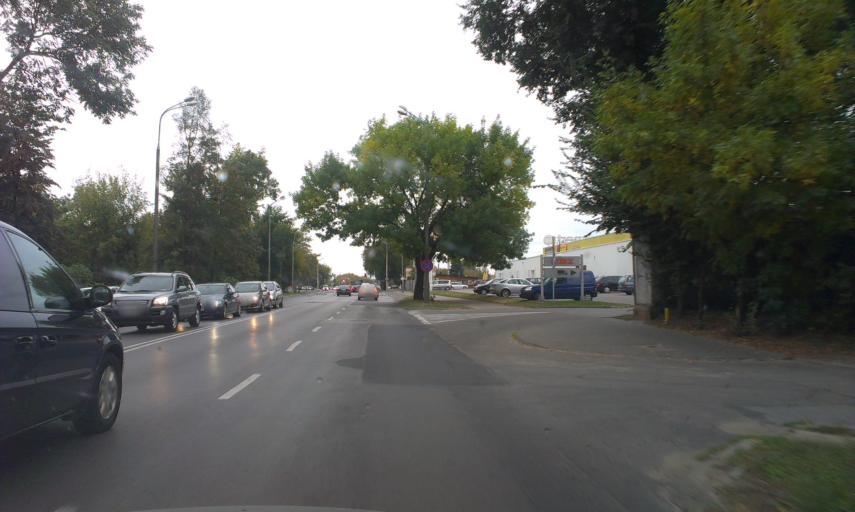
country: PL
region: Masovian Voivodeship
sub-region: Radom
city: Radom
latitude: 51.4065
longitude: 21.1415
